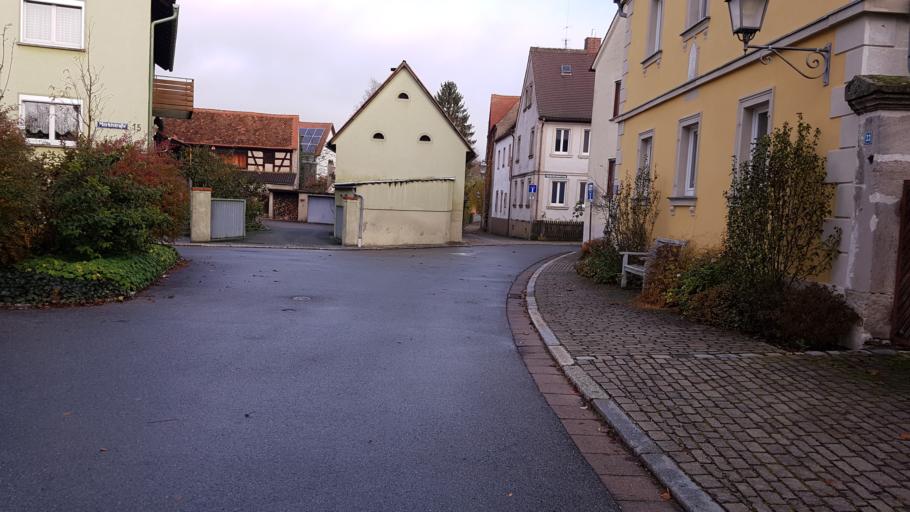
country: DE
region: Bavaria
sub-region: Upper Franconia
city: Burgebrach
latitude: 49.8285
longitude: 10.7438
